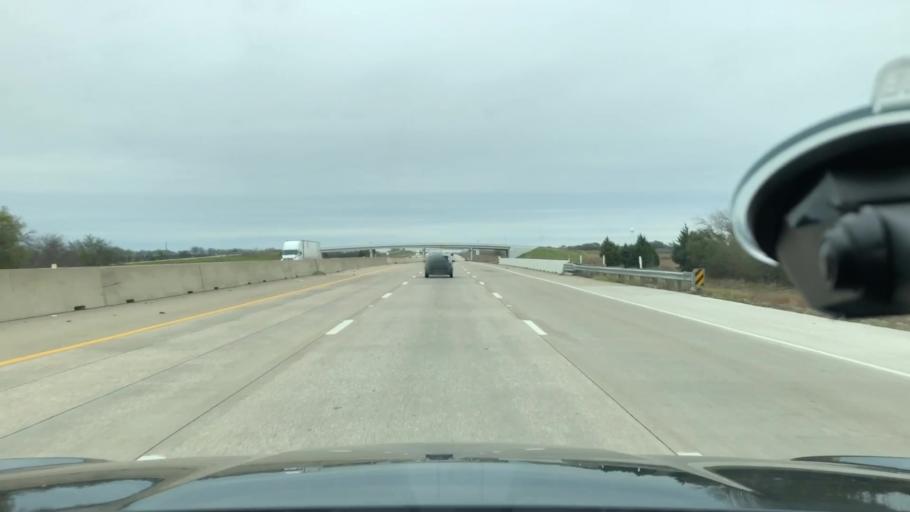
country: US
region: Texas
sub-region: Ellis County
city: Nash
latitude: 32.2872
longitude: -96.8673
